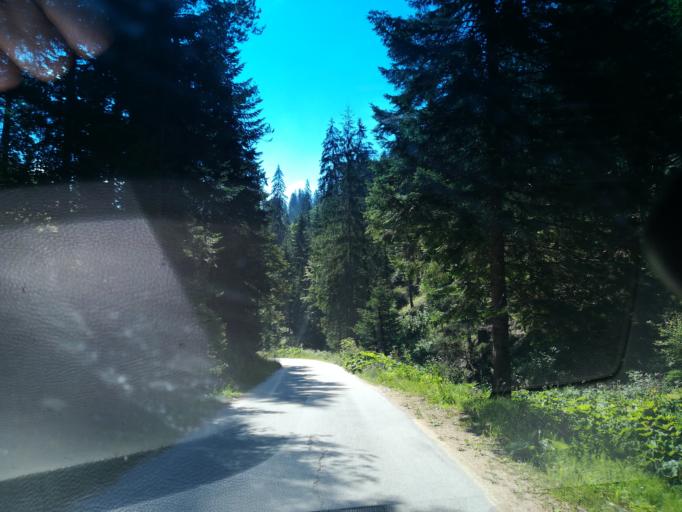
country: BG
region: Smolyan
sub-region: Obshtina Smolyan
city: Smolyan
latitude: 41.6603
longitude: 24.8060
